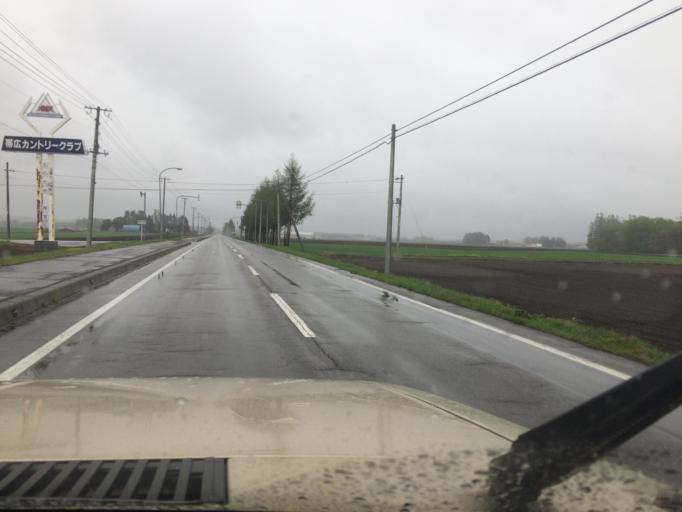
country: JP
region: Hokkaido
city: Obihiro
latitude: 42.8332
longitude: 142.9934
